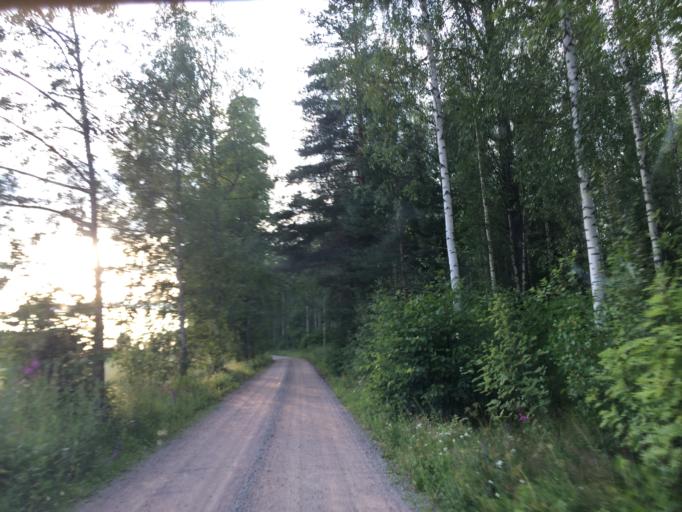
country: FI
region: Haeme
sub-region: Haemeenlinna
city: Janakkala
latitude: 60.8924
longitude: 24.6157
